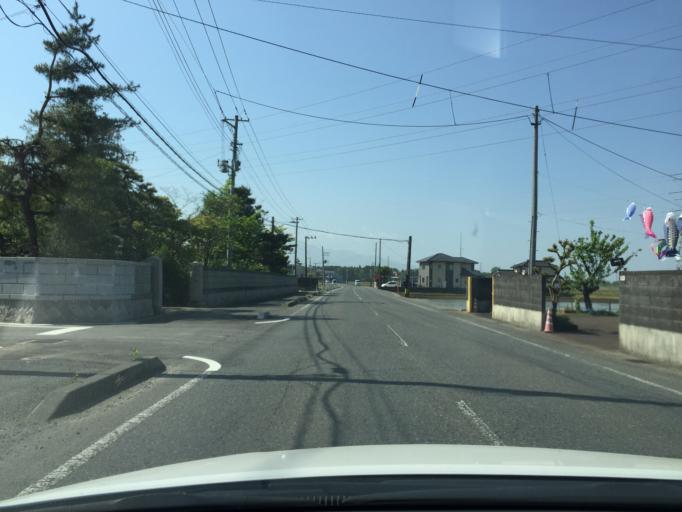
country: JP
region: Niigata
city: Gosen
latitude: 37.7461
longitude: 139.2036
